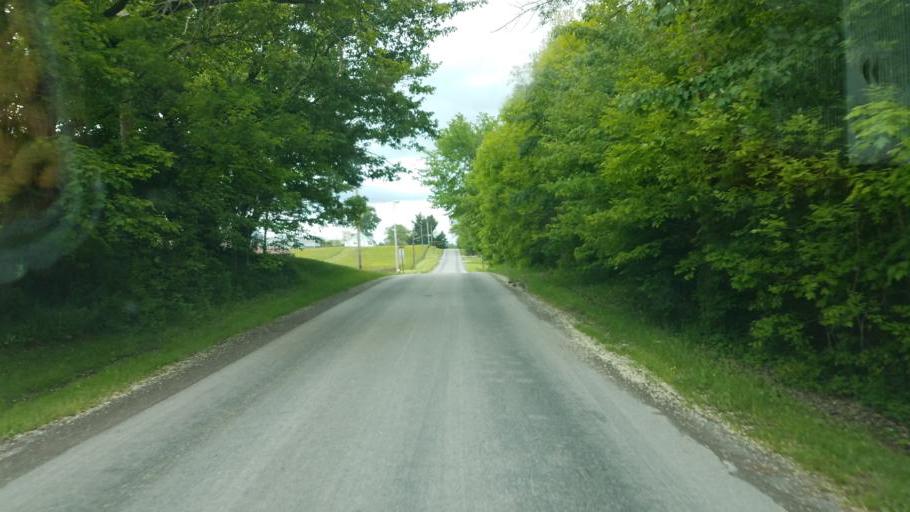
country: US
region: Ohio
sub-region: Geauga County
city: Middlefield
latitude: 41.3886
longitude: -80.9735
